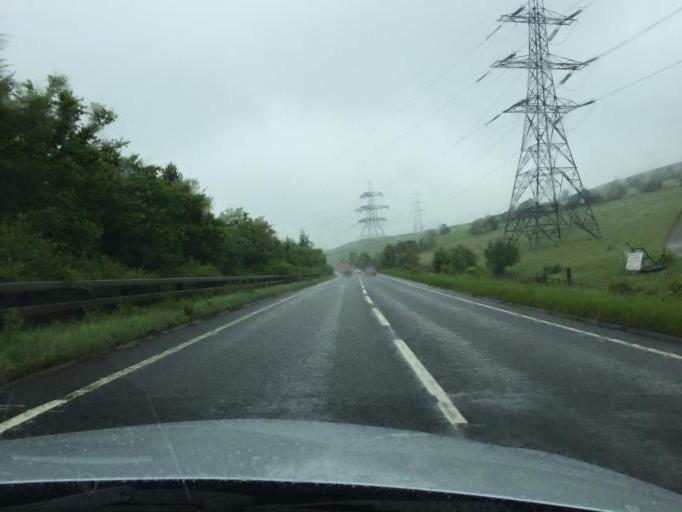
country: GB
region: England
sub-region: Sheffield
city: Stocksbridge
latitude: 53.4871
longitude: -1.5955
